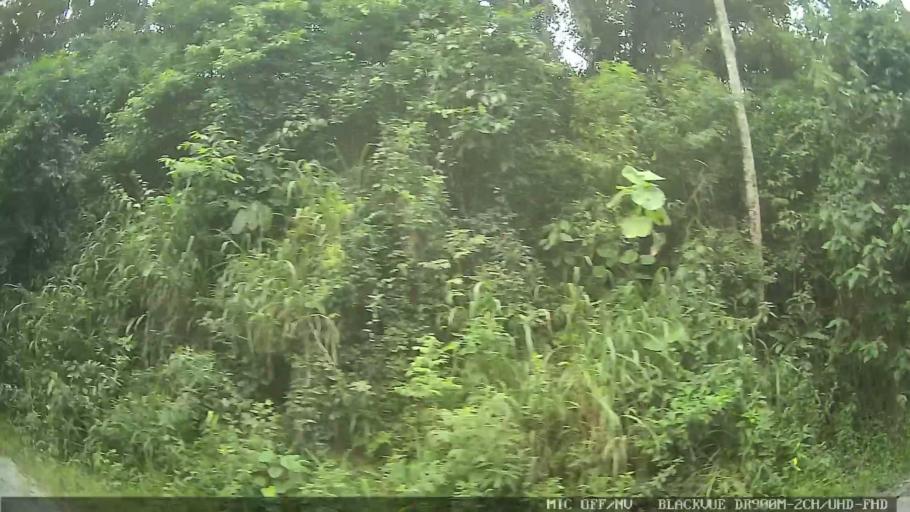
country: BR
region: Sao Paulo
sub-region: Aruja
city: Aruja
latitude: -23.4228
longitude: -46.2696
